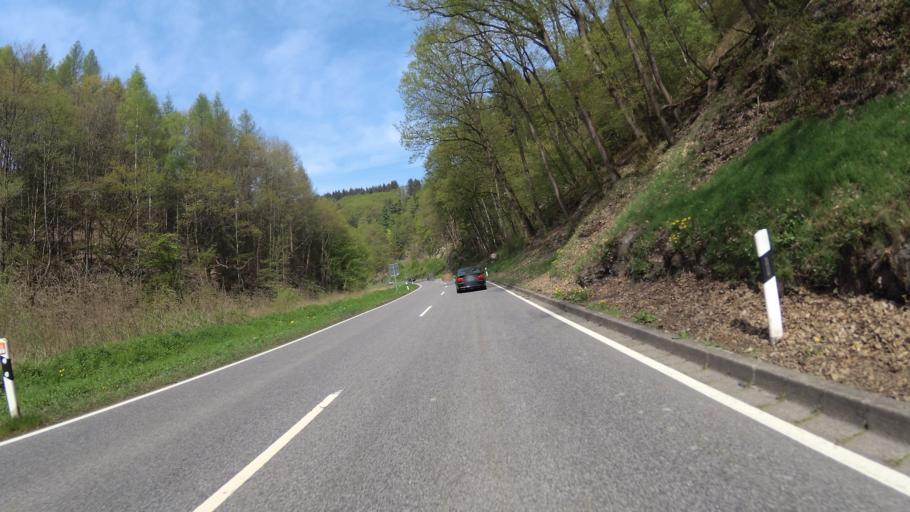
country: DE
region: Rheinland-Pfalz
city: Longkamp
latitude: 49.9023
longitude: 7.1003
